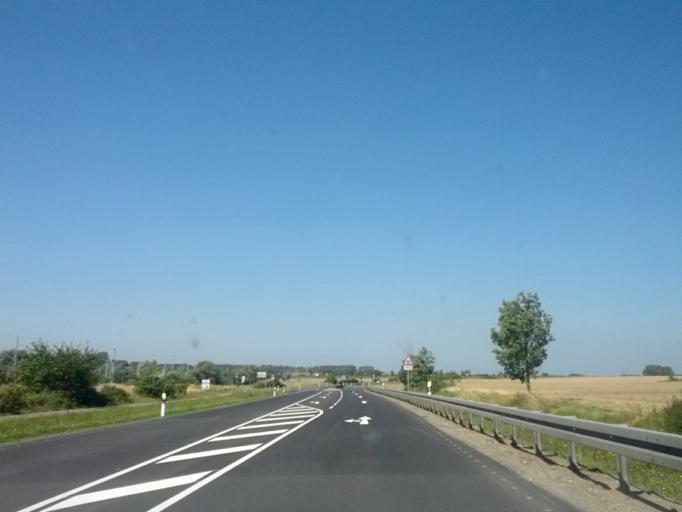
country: DE
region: Mecklenburg-Vorpommern
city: Sagard
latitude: 54.5048
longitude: 13.5506
